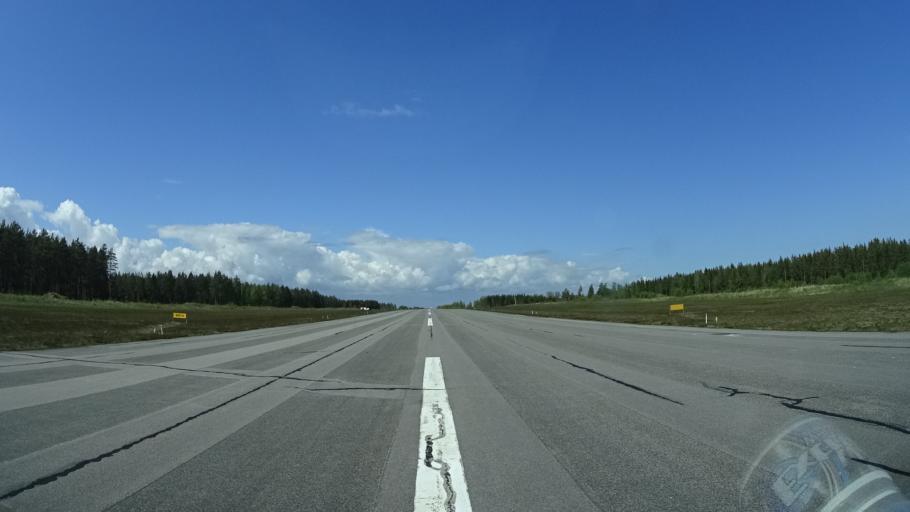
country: SE
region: Kalmar
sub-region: Vasterviks Kommun
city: Vaestervik
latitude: 57.7780
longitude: 16.5260
